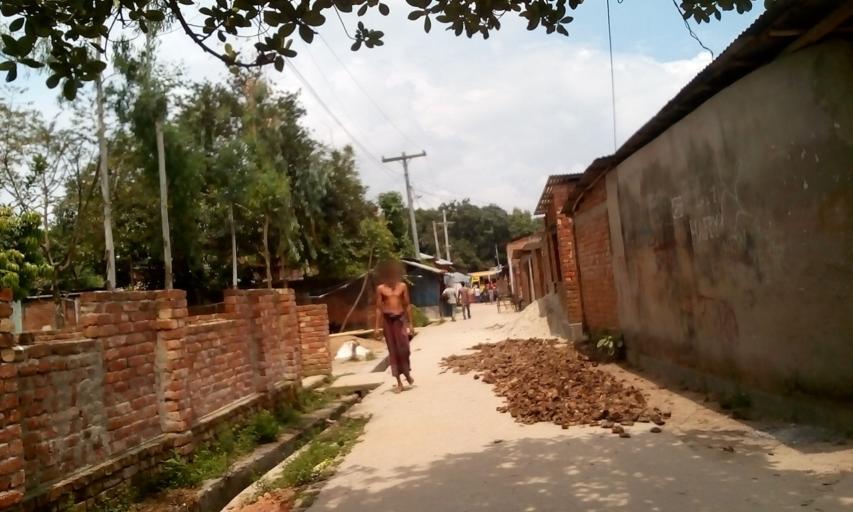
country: IN
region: West Bengal
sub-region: Dakshin Dinajpur
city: Balurghat
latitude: 25.3920
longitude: 88.9901
